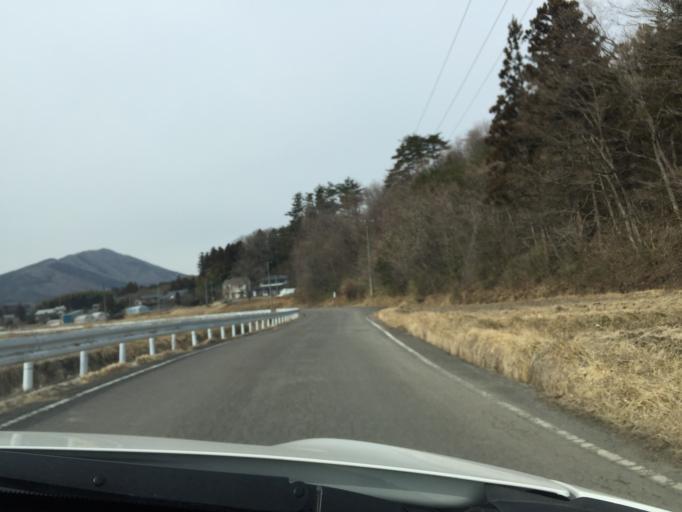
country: JP
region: Fukushima
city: Ishikawa
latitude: 37.2414
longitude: 140.5648
